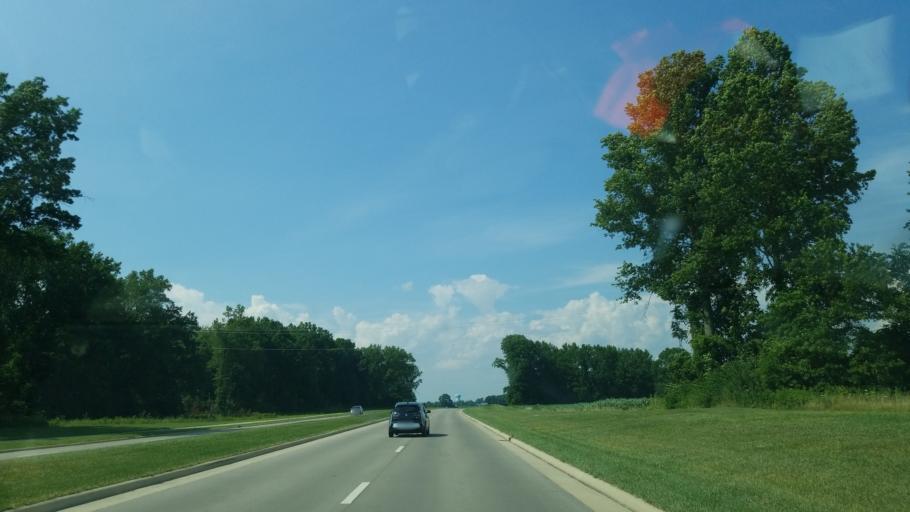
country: US
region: Ohio
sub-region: Delaware County
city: Delaware
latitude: 40.2570
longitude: -83.0912
